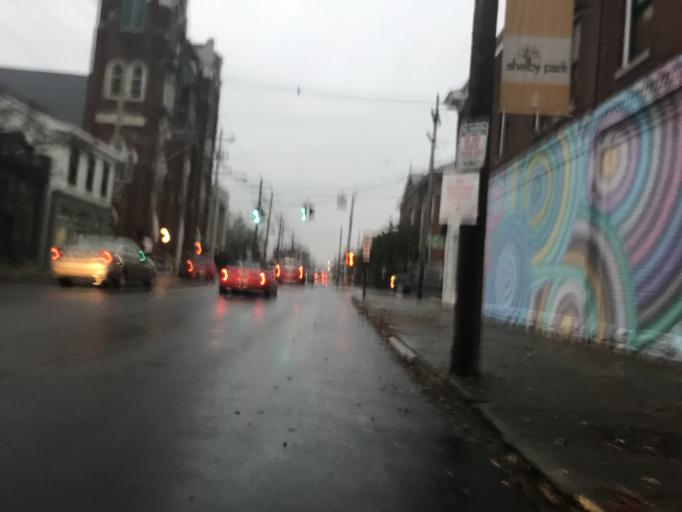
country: US
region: Kentucky
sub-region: Jefferson County
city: Louisville
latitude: 38.2338
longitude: -85.7415
